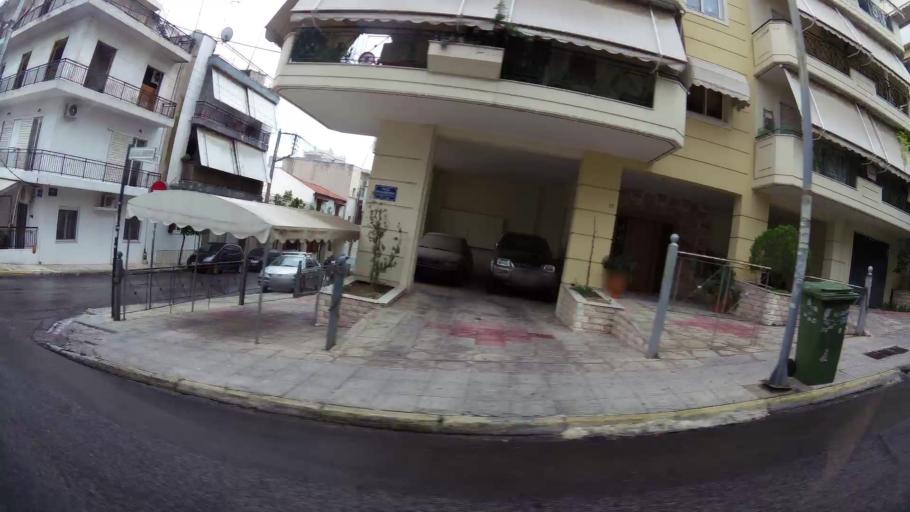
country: GR
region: Attica
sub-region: Nomos Piraios
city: Korydallos
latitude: 37.9855
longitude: 23.6457
